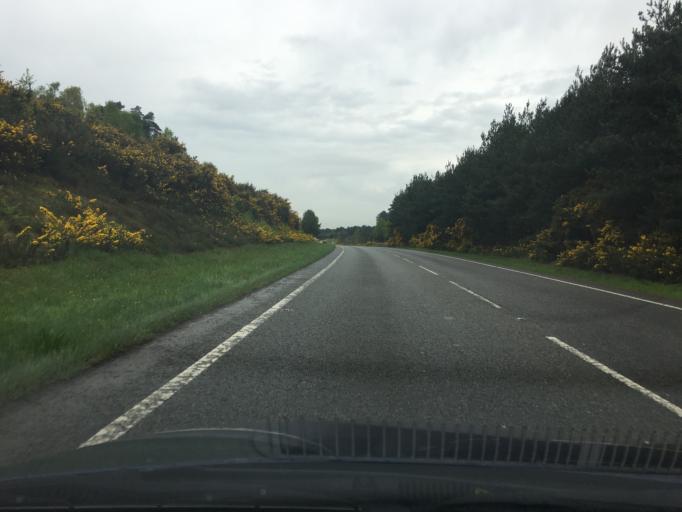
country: GB
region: England
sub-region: Bracknell Forest
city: Crowthorne
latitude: 51.3738
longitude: -0.7666
